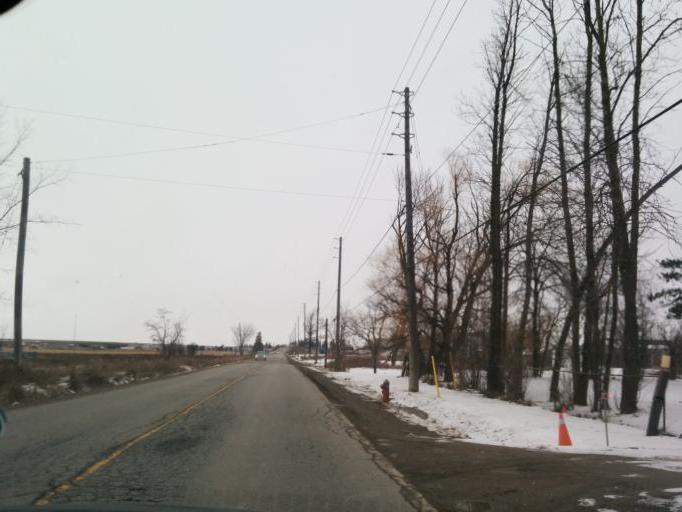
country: CA
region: Ontario
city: Brampton
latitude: 43.5849
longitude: -79.8013
